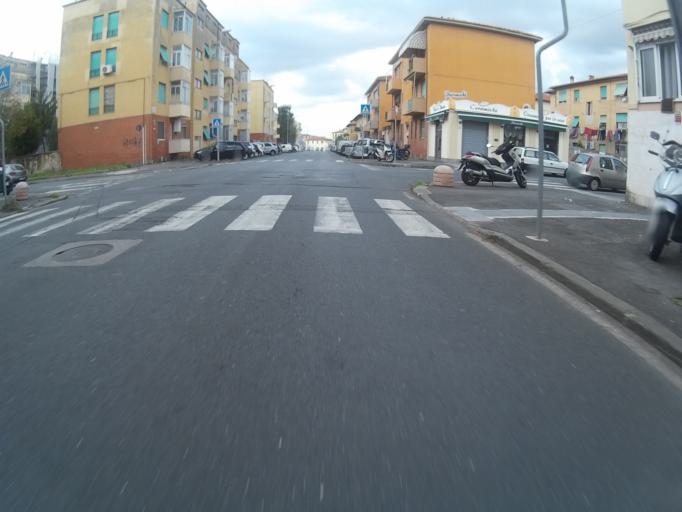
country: IT
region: Tuscany
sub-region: Provincia di Livorno
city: Livorno
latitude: 43.5611
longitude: 10.3318
